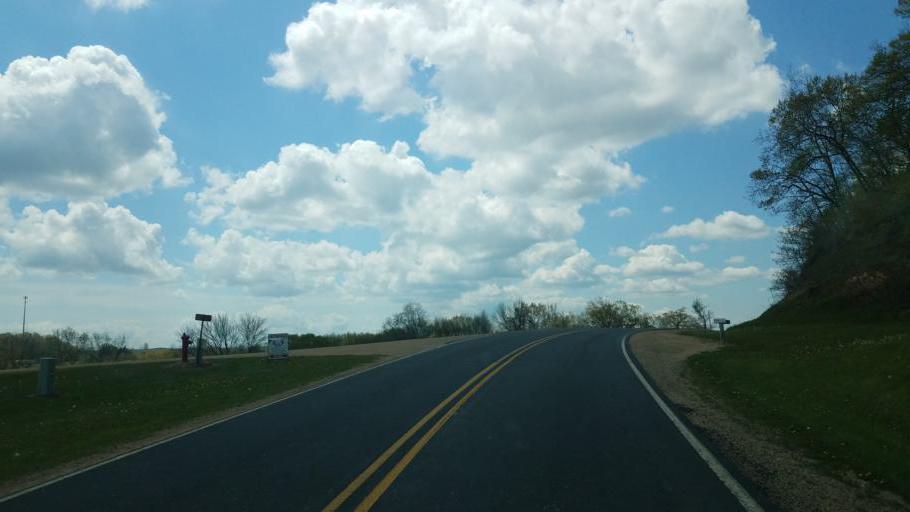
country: US
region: Wisconsin
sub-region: Vernon County
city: Hillsboro
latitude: 43.6708
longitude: -90.3501
